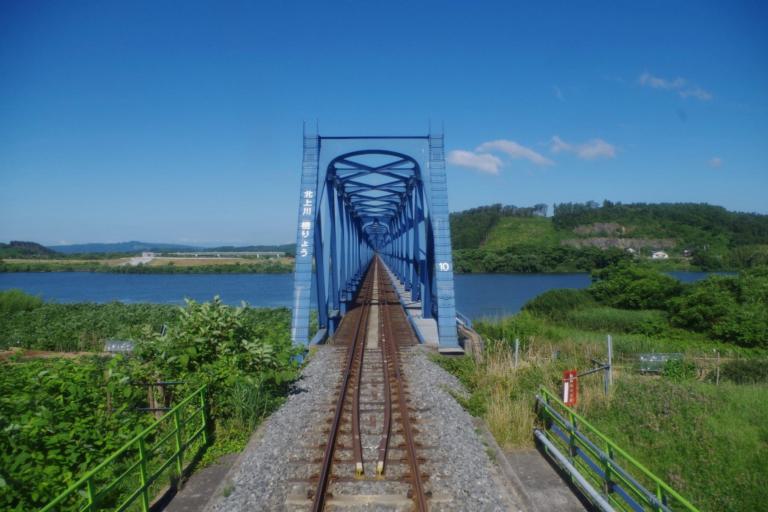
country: JP
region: Miyagi
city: Wakuya
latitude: 38.6089
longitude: 141.3001
